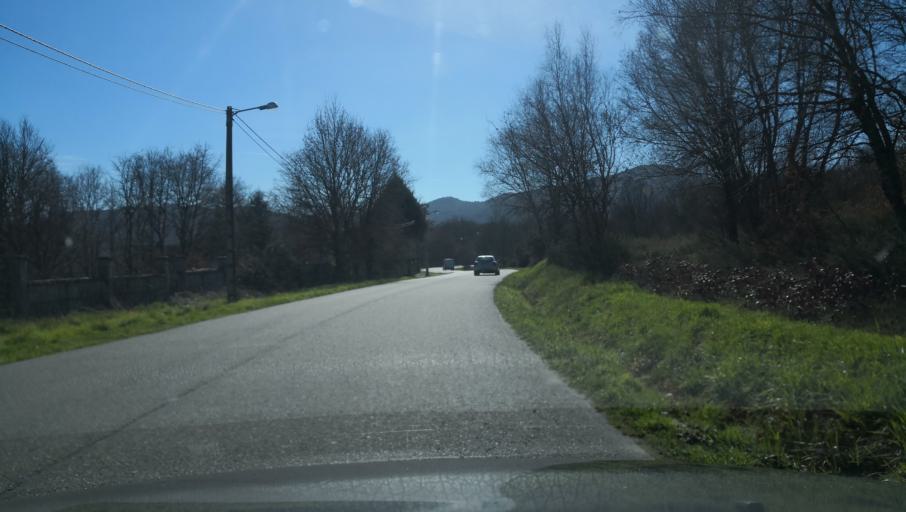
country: ES
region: Galicia
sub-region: Provincia de Ourense
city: Allariz
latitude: 42.2003
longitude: -7.8070
